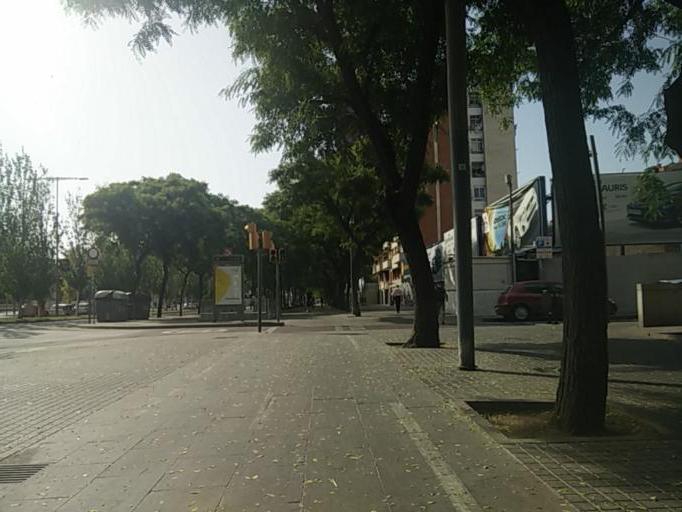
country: ES
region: Catalonia
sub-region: Provincia de Barcelona
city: Sants-Montjuic
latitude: 41.3781
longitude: 2.1455
